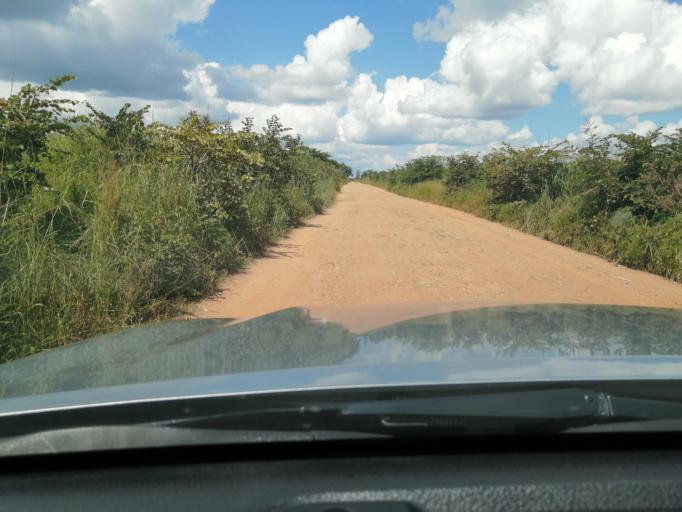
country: ZM
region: Lusaka
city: Lusaka
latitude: -15.1996
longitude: 28.0253
